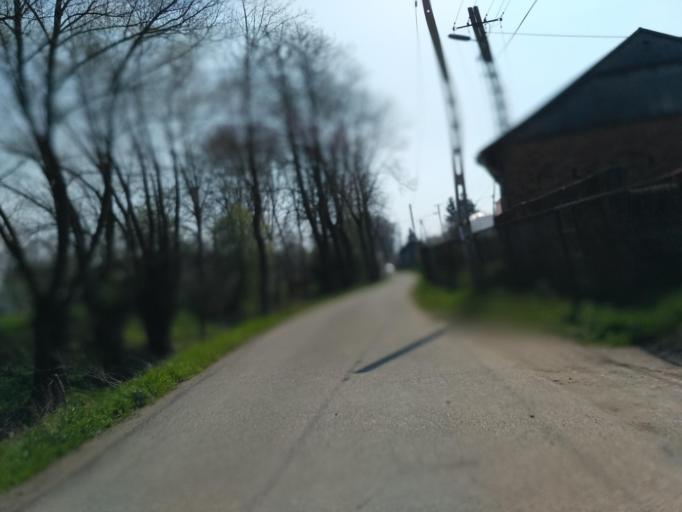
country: PL
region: Subcarpathian Voivodeship
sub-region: Powiat sanocki
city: Zarszyn
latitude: 49.6157
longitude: 22.0131
